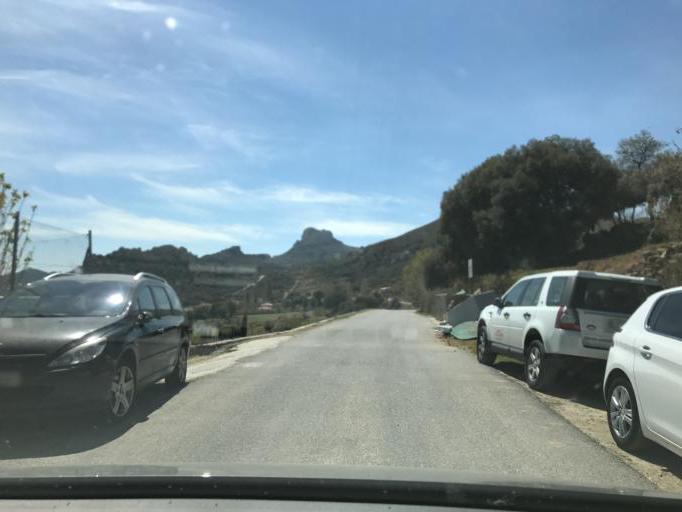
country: ES
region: Andalusia
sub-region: Provincia de Granada
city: Iznalloz
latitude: 37.3218
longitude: -3.4535
